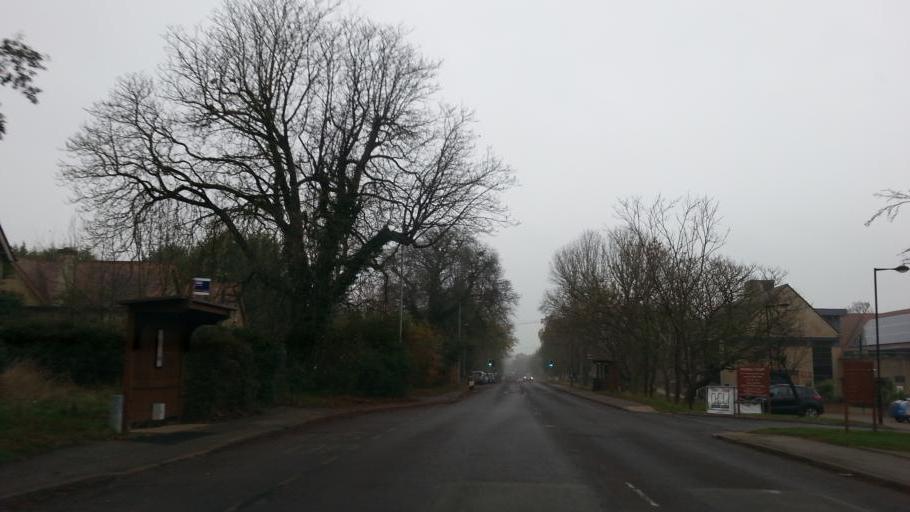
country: GB
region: England
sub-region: Cambridgeshire
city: Papworth Everard
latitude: 52.2504
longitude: -0.1189
